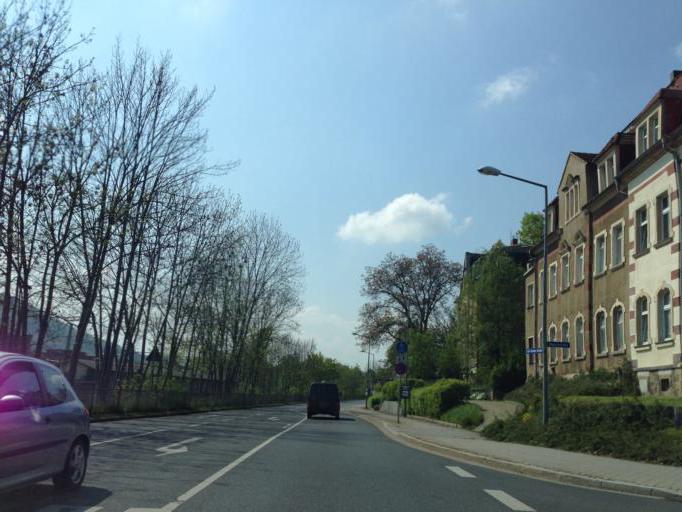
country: DE
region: Saxony
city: Freital
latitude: 51.0142
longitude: 13.6615
